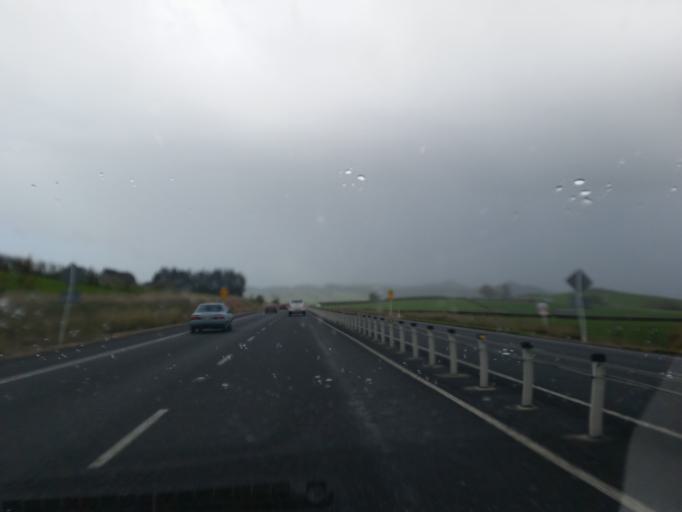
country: NZ
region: Waikato
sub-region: Waikato District
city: Te Kauwhata
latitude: -37.2803
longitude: 175.2981
